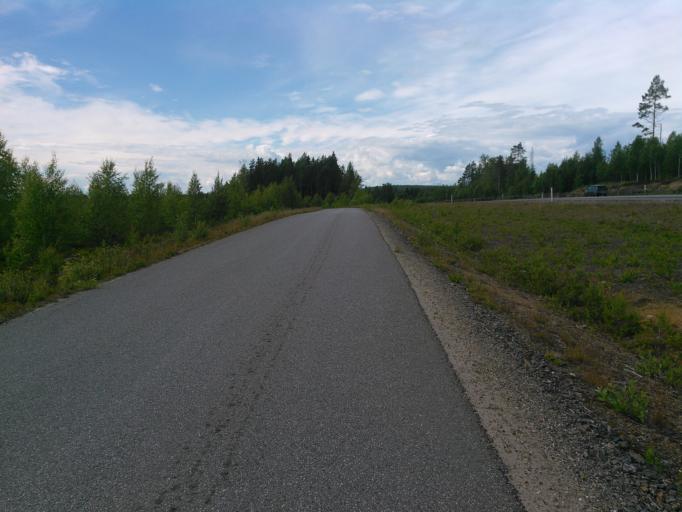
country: SE
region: Vaesterbotten
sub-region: Vannas Kommun
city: Vannasby
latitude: 63.8918
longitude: 19.9884
